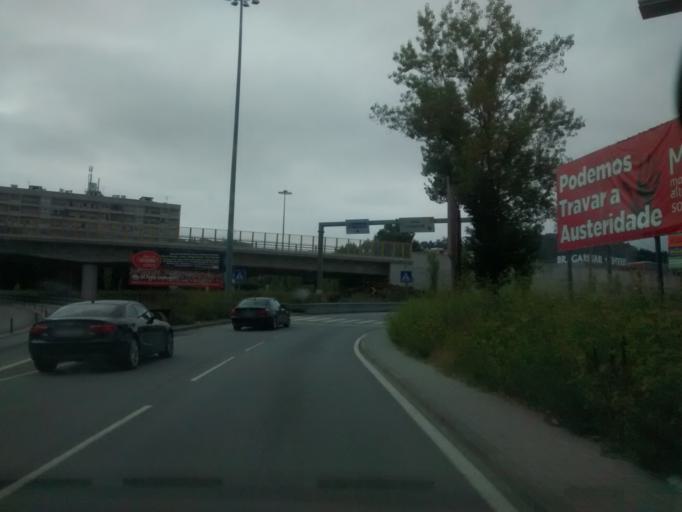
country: PT
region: Braga
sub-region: Braga
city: Braga
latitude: 41.5621
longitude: -8.4076
